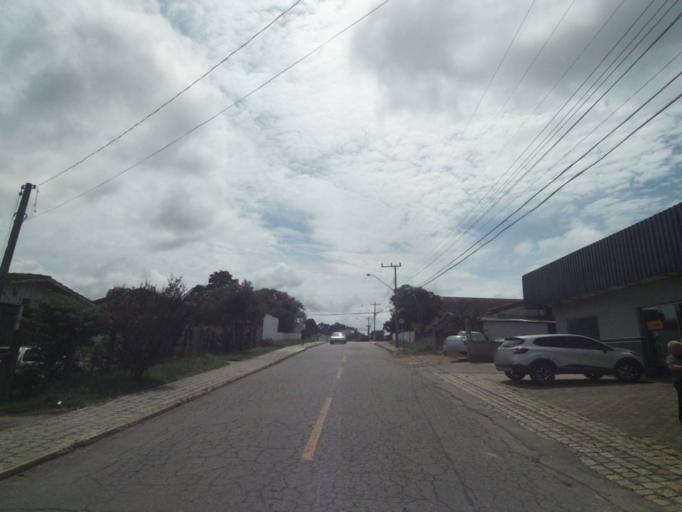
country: BR
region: Parana
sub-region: Campina Grande Do Sul
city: Campina Grande do Sul
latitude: -25.3068
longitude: -49.0545
